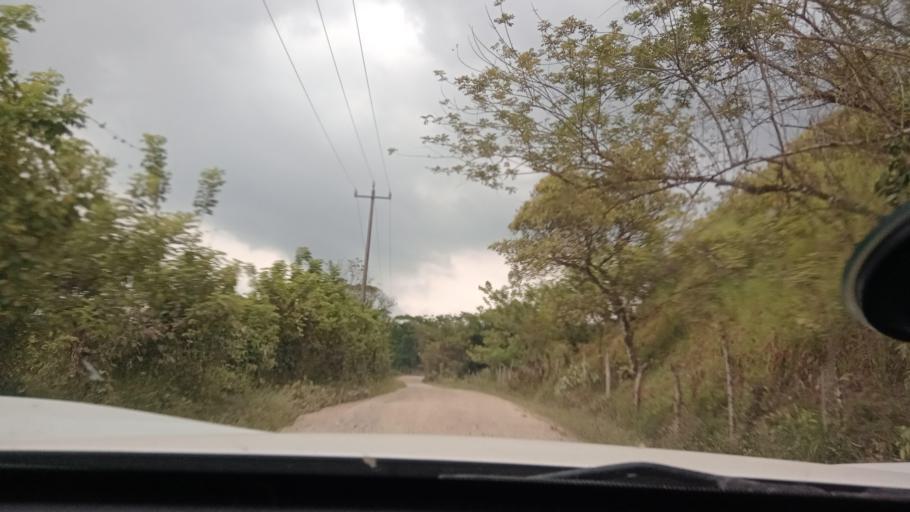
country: MX
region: Tabasco
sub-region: Huimanguillo
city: Francisco Rueda
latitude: 17.4406
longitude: -94.0655
